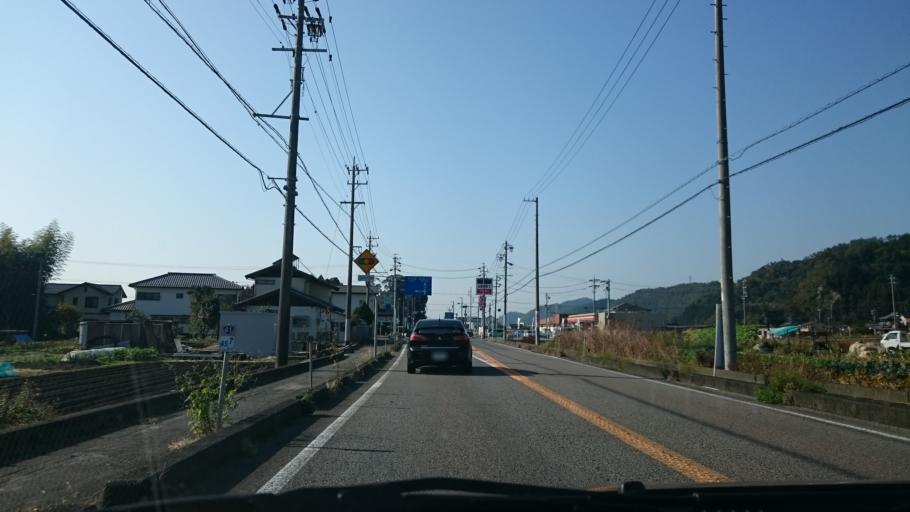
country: JP
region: Gifu
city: Minokamo
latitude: 35.5096
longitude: 137.0829
